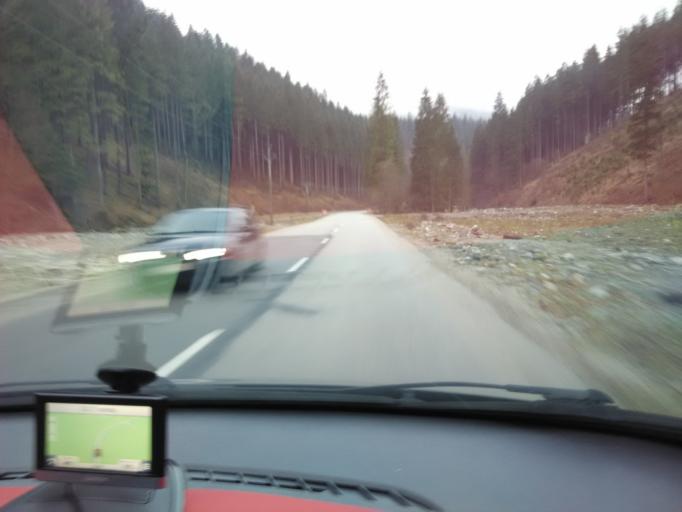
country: SK
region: Zilinsky
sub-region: Okres Zilina
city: Terchova
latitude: 49.2205
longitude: 19.0336
